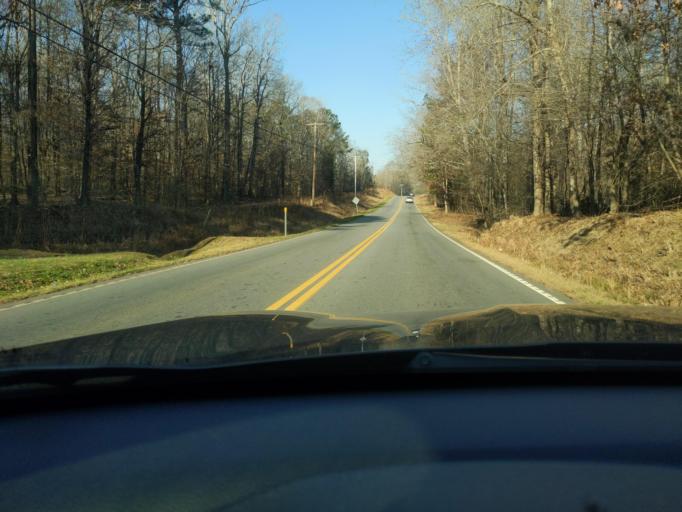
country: US
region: South Carolina
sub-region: Greenwood County
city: Greenwood
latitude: 34.1907
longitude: -82.1207
